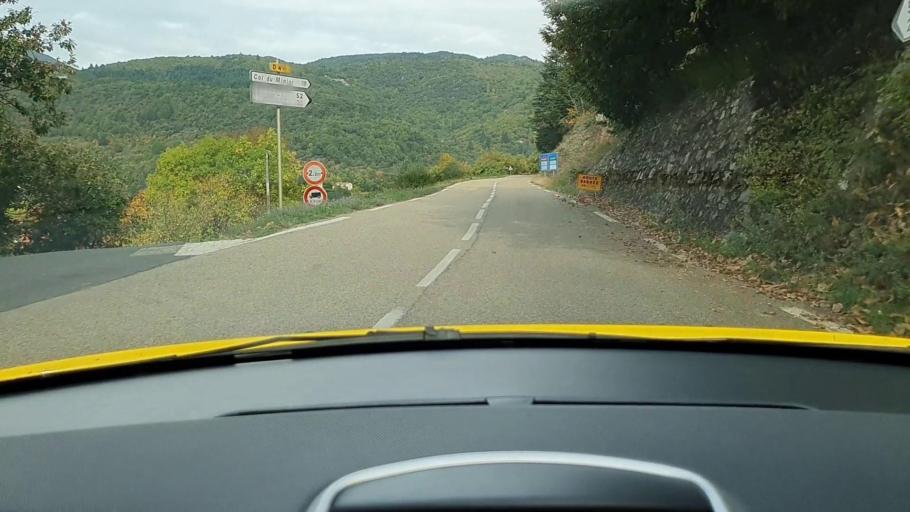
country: FR
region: Languedoc-Roussillon
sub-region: Departement du Gard
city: Le Vigan
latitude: 43.9979
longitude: 3.5894
